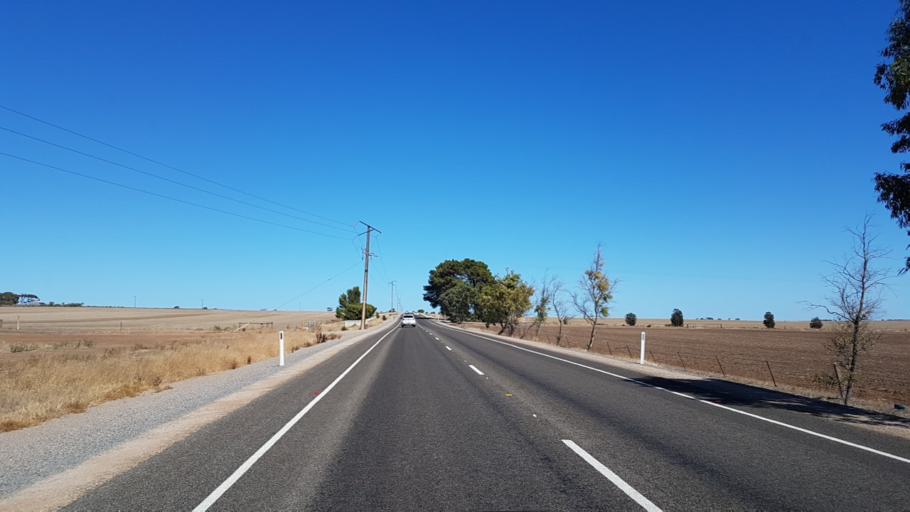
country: AU
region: South Australia
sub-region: Copper Coast
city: Kadina
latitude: -34.0437
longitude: 137.9369
